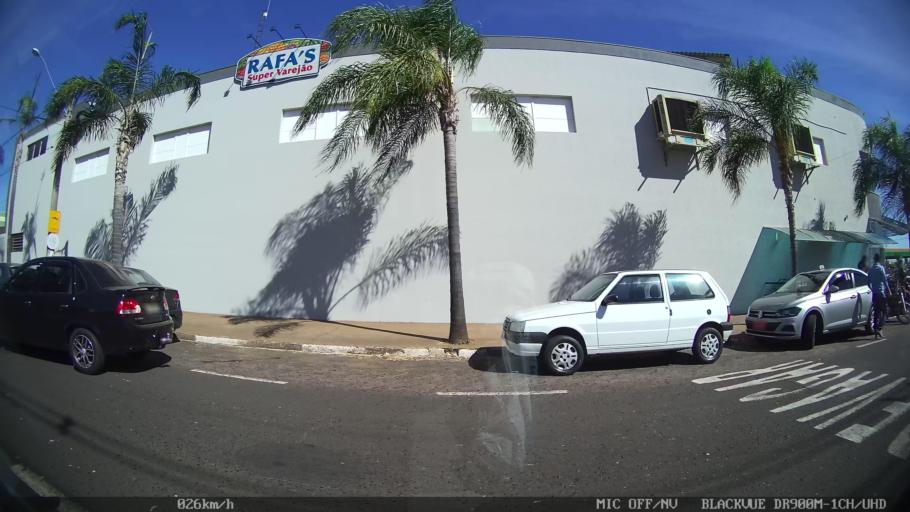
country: BR
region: Sao Paulo
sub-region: Franca
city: Franca
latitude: -20.5426
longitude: -47.3753
